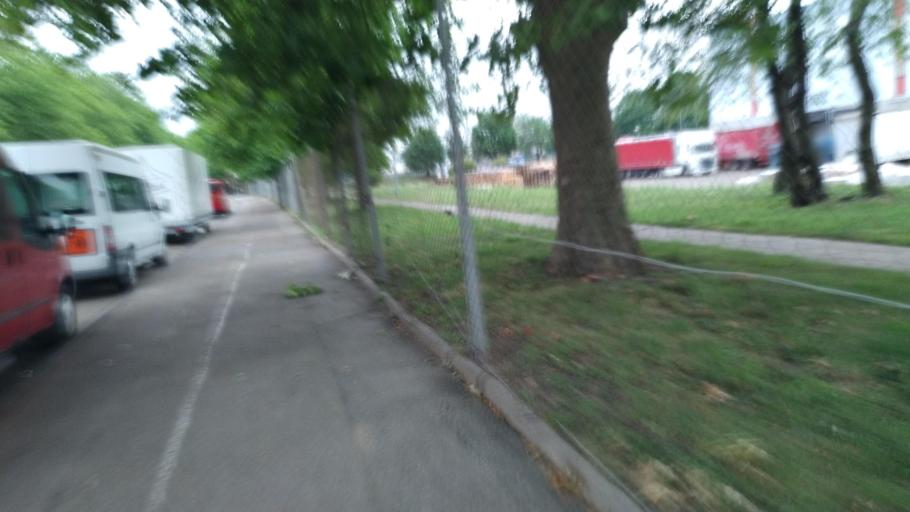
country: DE
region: Baden-Wuerttemberg
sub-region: Karlsruhe Region
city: Ettlingen
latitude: 48.9442
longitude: 8.3820
